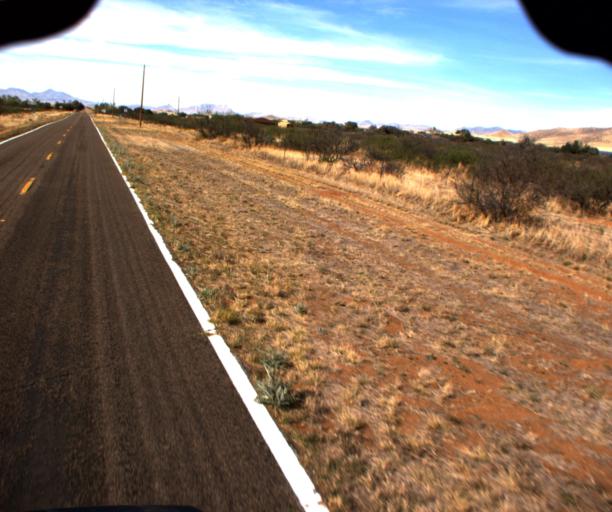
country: US
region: Arizona
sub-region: Cochise County
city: Willcox
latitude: 31.8813
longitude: -109.4913
